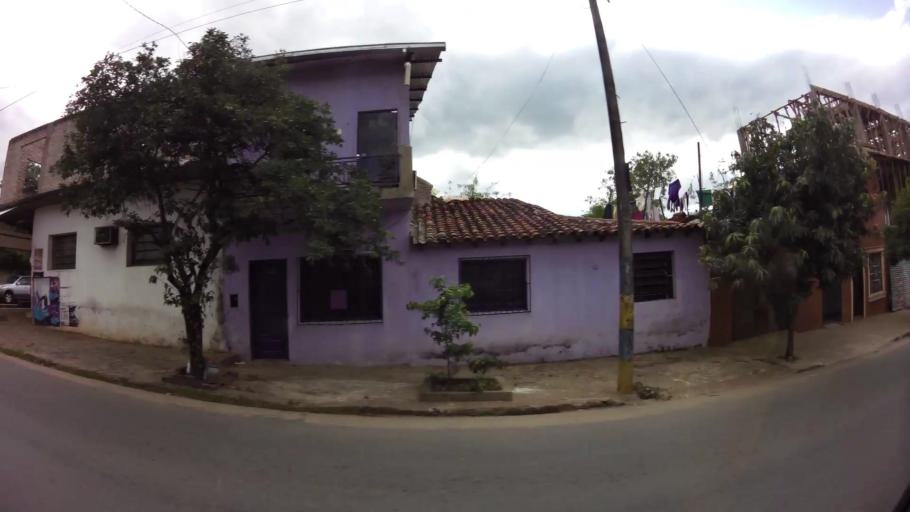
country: PY
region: Central
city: San Lorenzo
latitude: -25.2671
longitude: -57.5015
